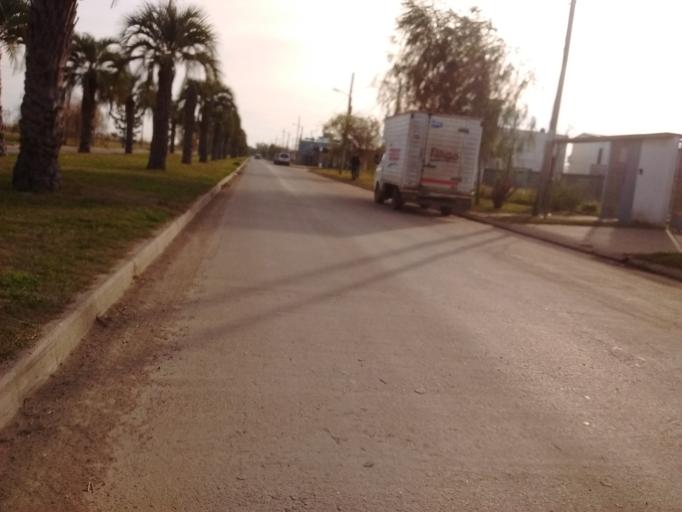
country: AR
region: Santa Fe
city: Roldan
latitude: -32.9319
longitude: -60.8951
